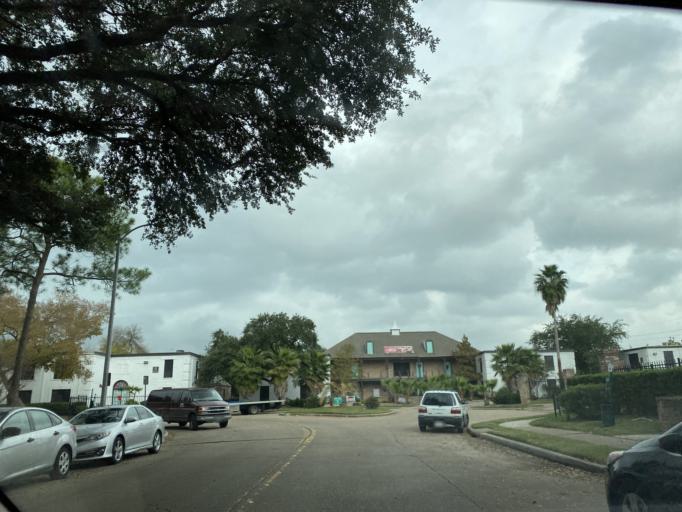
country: US
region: Texas
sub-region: Harris County
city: Piney Point Village
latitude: 29.7421
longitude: -95.4966
